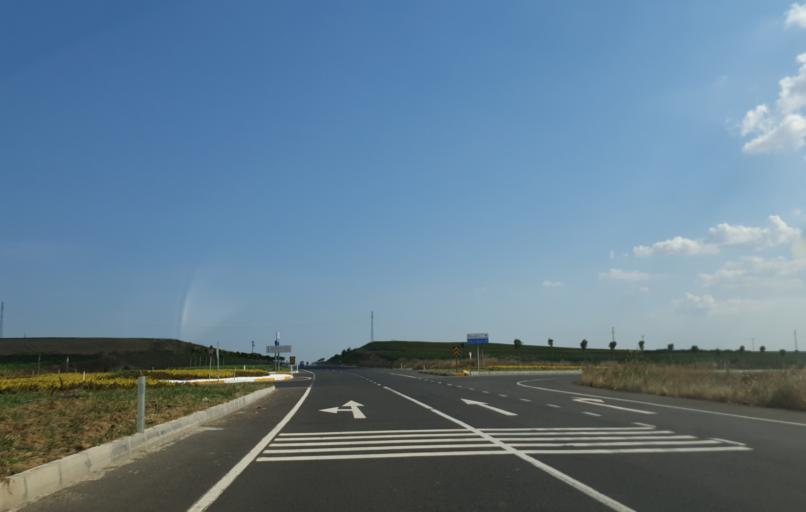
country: TR
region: Tekirdag
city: Muratli
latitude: 41.2113
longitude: 27.5341
